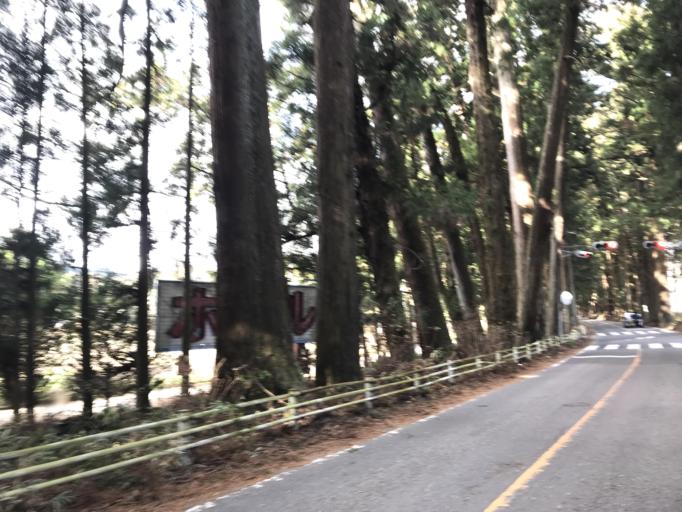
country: JP
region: Tochigi
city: Imaichi
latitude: 36.6894
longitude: 139.7173
